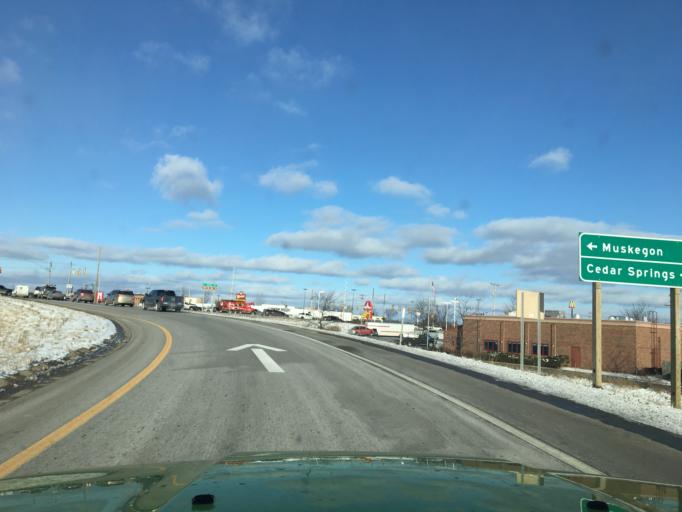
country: US
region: Michigan
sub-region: Kent County
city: Cedar Springs
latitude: 43.2186
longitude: -85.5726
